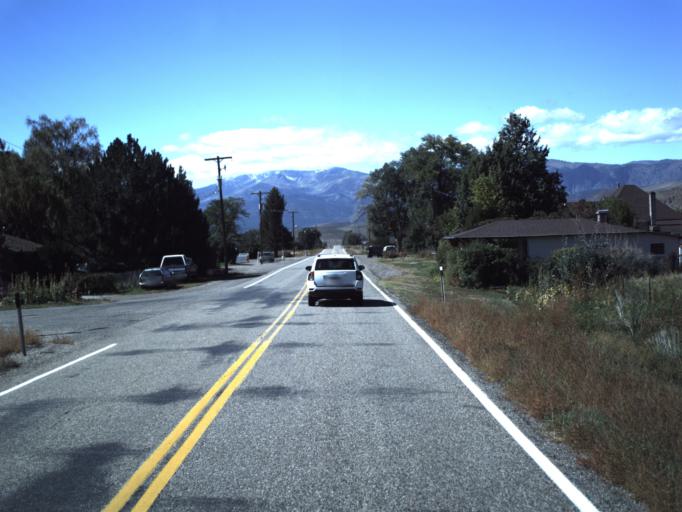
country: US
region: Utah
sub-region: Piute County
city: Junction
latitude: 38.2083
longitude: -112.1851
